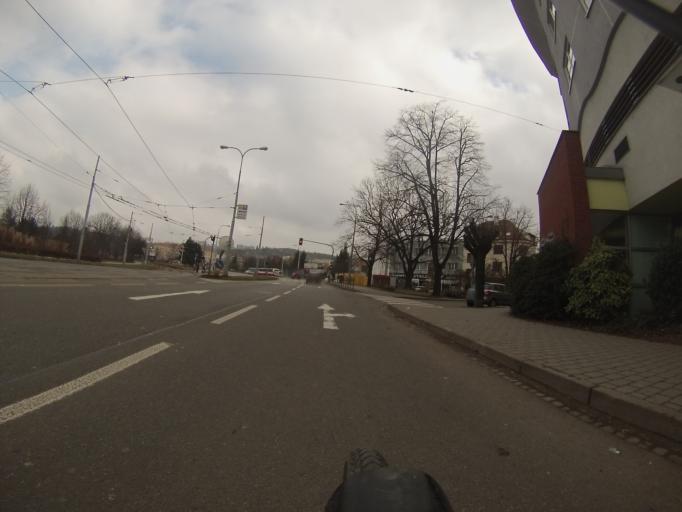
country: CZ
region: South Moravian
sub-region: Mesto Brno
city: Brno
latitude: 49.2011
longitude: 16.6394
